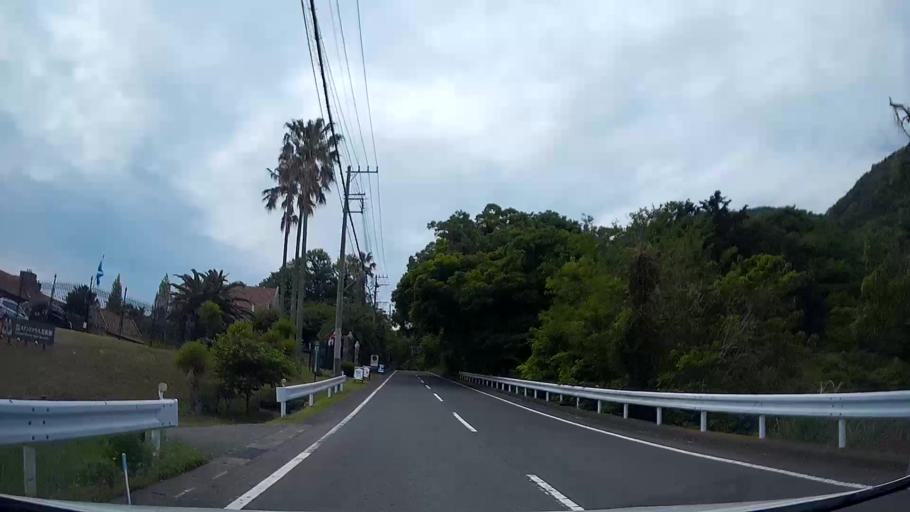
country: JP
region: Shizuoka
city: Ito
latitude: 34.9436
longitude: 139.1372
